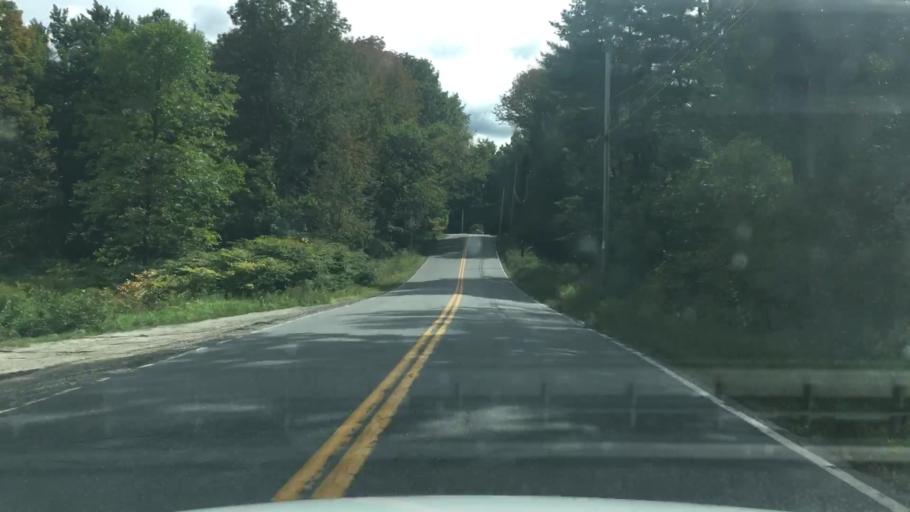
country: US
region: Maine
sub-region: Androscoggin County
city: Lewiston
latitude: 44.0295
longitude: -70.1838
